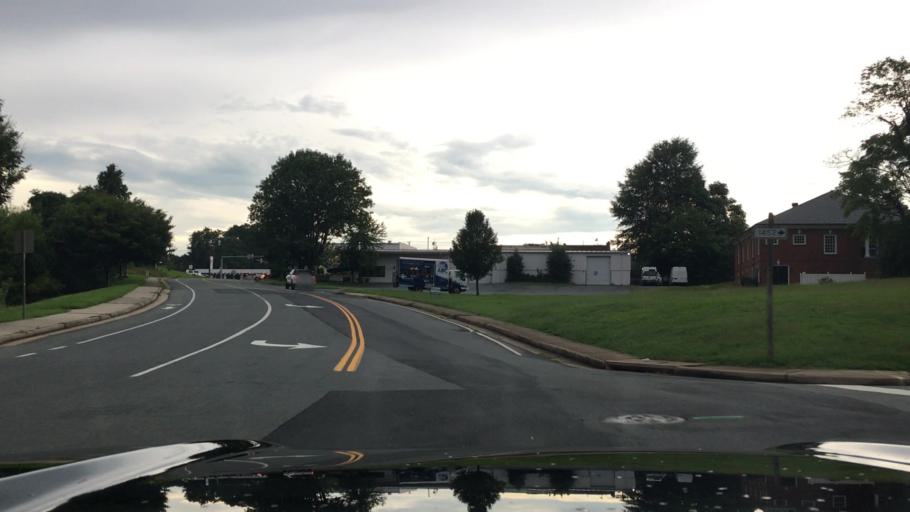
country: US
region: Virginia
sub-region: City of Charlottesville
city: Charlottesville
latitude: 38.0695
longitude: -78.4818
